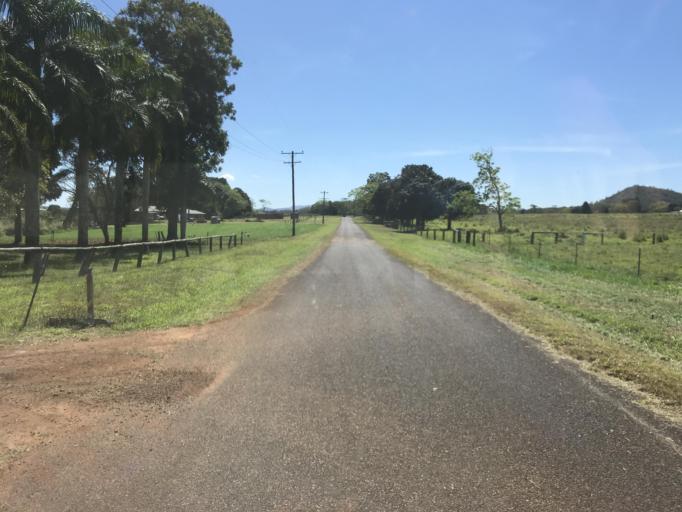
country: AU
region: Queensland
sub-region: Tablelands
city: Atherton
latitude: -17.2791
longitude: 145.5442
